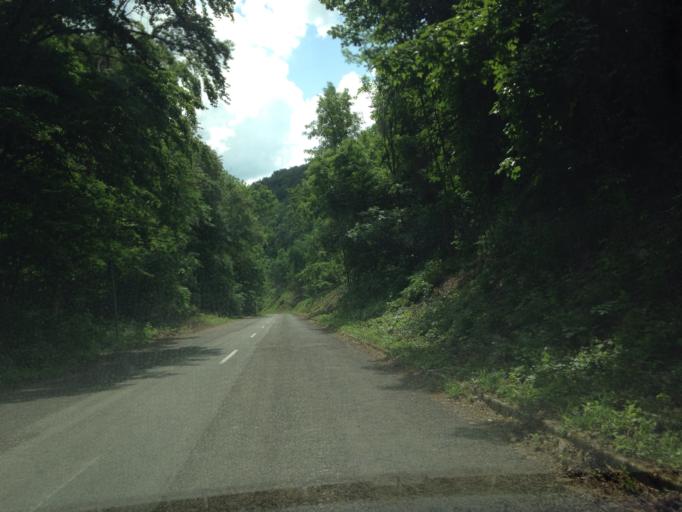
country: HU
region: Pest
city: Visegrad
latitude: 47.7511
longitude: 18.9426
